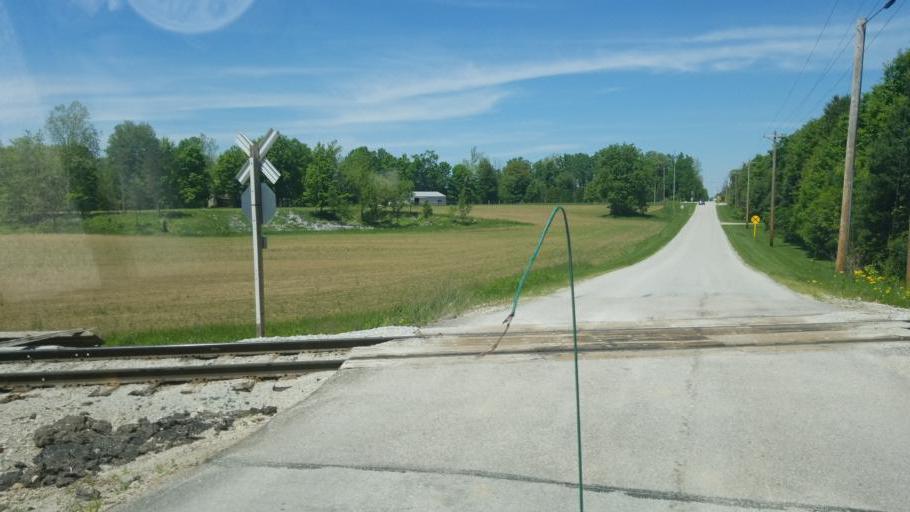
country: US
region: Ohio
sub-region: Huron County
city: Greenwich
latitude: 41.0323
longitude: -82.5356
